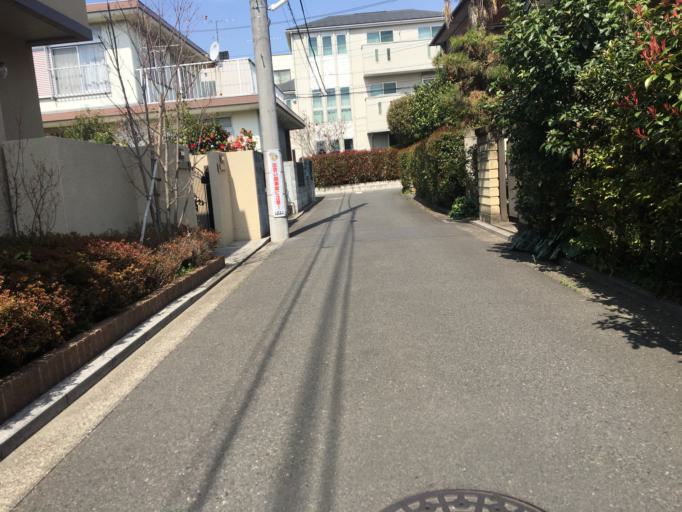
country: JP
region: Tokyo
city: Kamirenjaku
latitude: 35.6975
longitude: 139.5431
